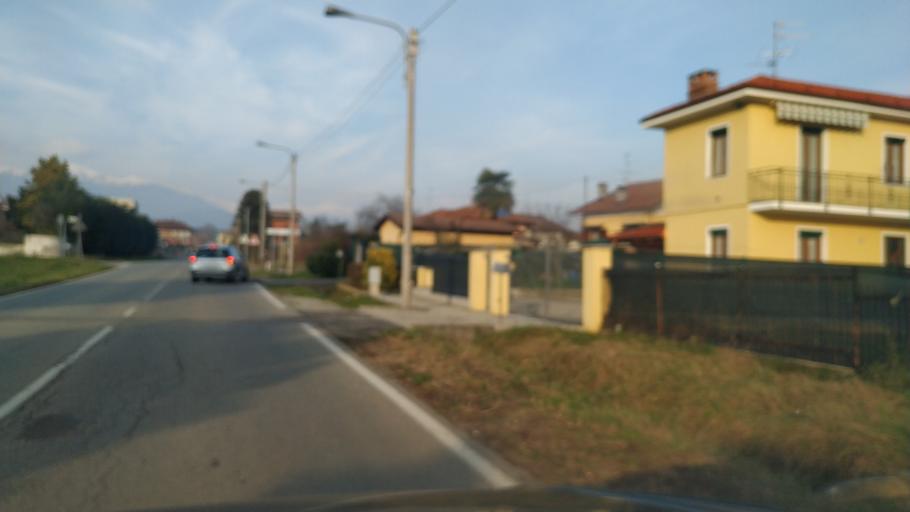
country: IT
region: Piedmont
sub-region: Provincia di Biella
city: Mongrando
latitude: 45.5283
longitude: 8.0107
